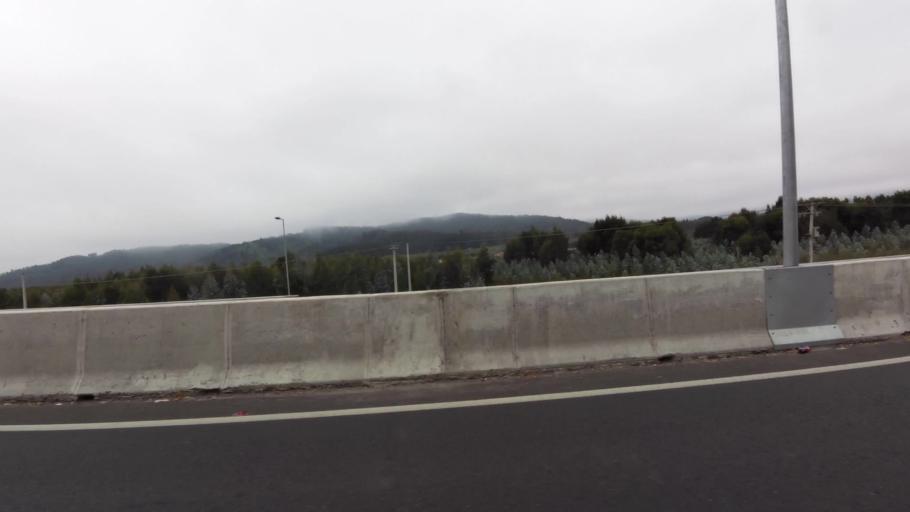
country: CL
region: Biobio
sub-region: Provincia de Concepcion
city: Concepcion
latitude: -36.8208
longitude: -72.9950
